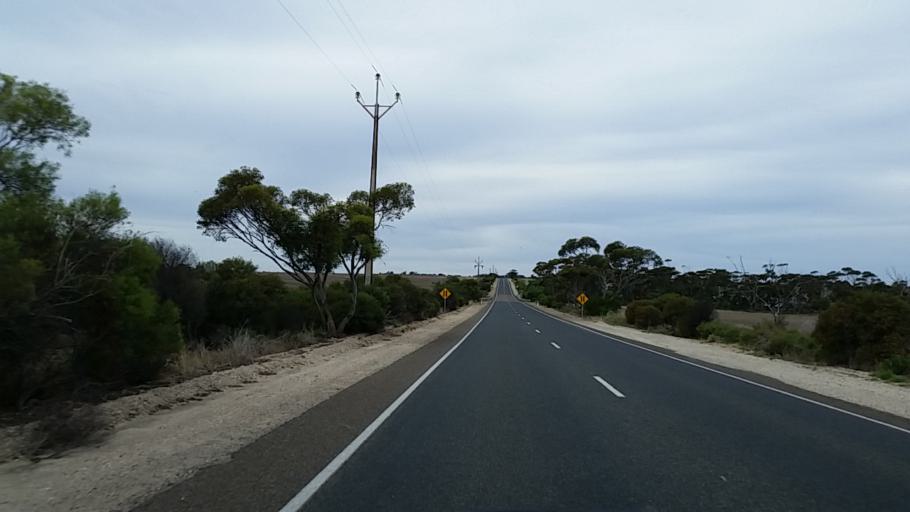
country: AU
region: South Australia
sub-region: Mid Murray
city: Mannum
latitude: -34.9138
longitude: 139.2681
